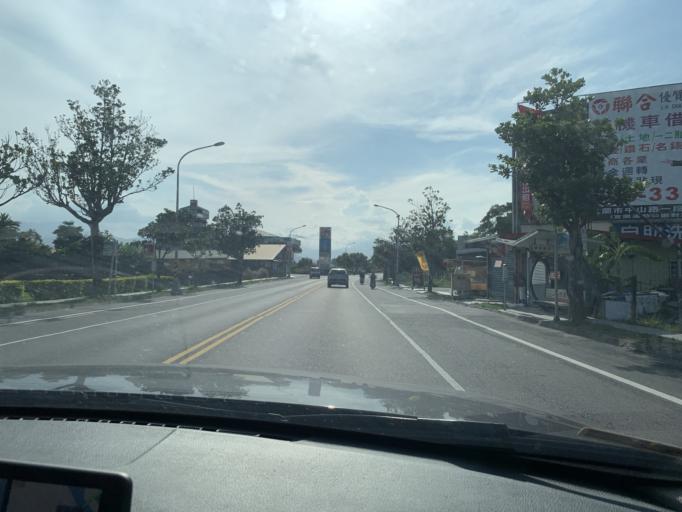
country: TW
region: Taiwan
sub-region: Yilan
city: Yilan
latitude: 24.6681
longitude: 121.8180
